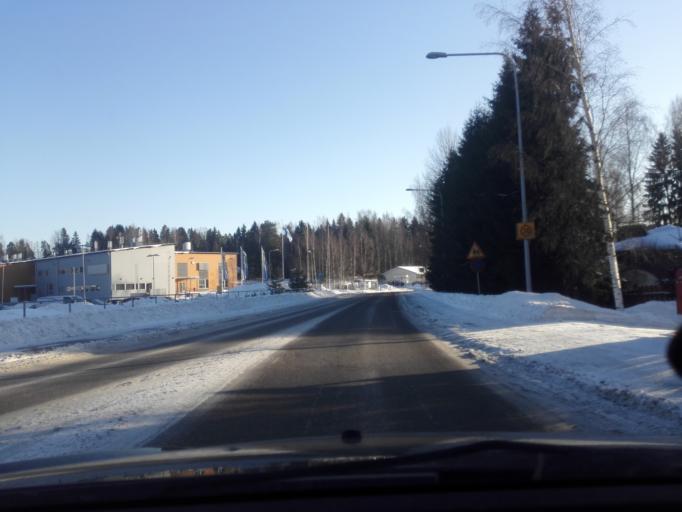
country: FI
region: Uusimaa
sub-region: Helsinki
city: Kerava
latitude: 60.3460
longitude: 25.1320
